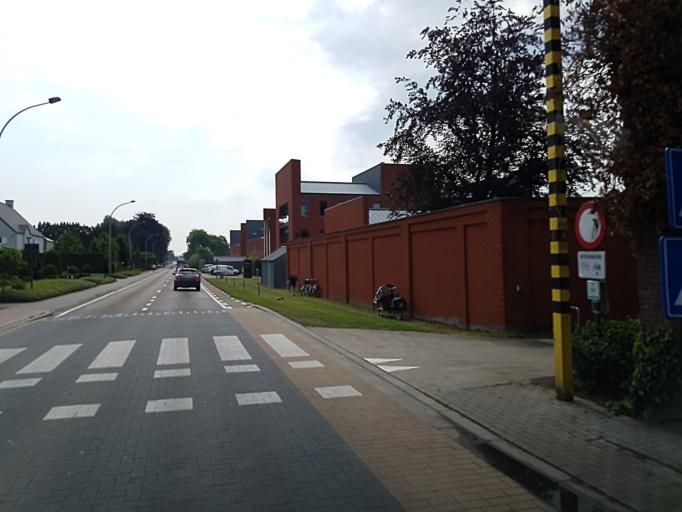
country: BE
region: Flanders
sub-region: Provincie Antwerpen
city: Mol
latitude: 51.1831
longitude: 5.1166
